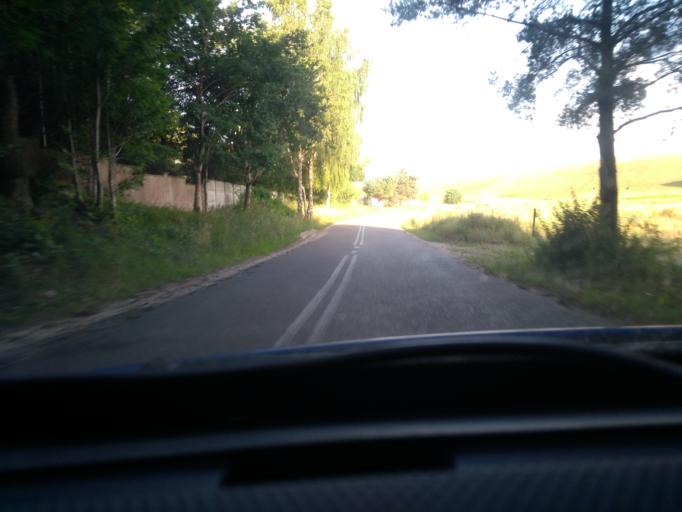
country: PL
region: Pomeranian Voivodeship
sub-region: Powiat kartuski
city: Zukowo
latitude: 54.3930
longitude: 18.3427
